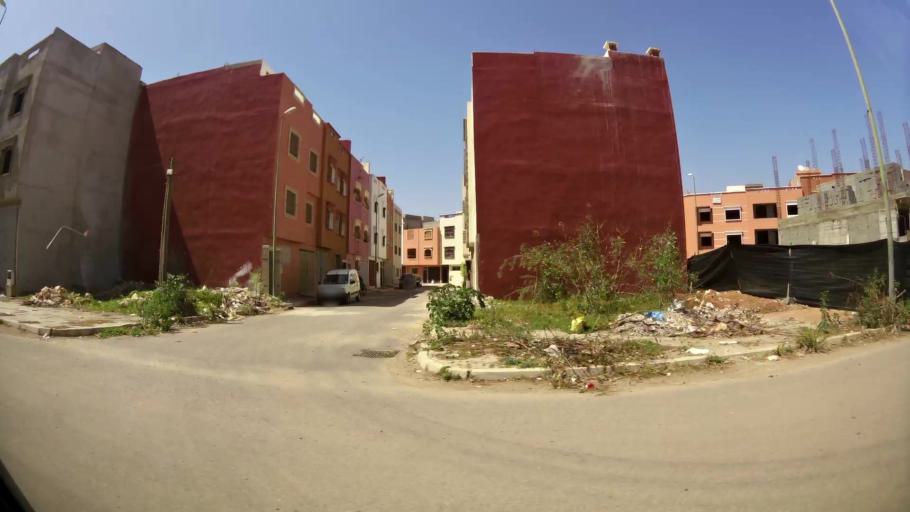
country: MA
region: Souss-Massa-Draa
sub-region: Inezgane-Ait Mellou
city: Inezgane
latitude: 30.3439
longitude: -9.5161
